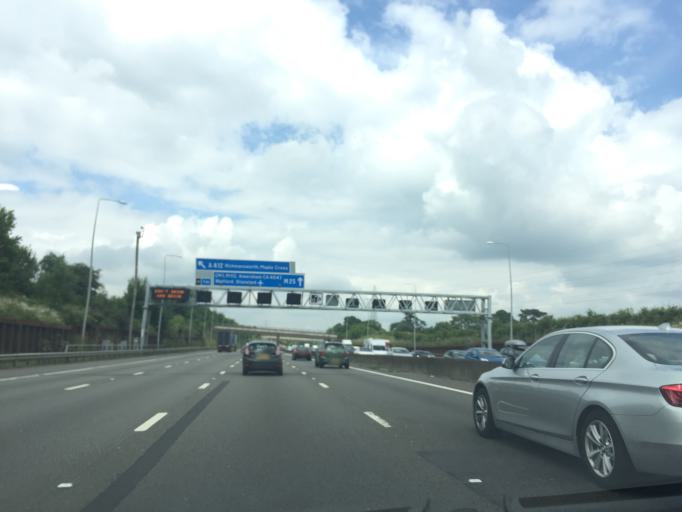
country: GB
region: England
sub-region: Buckinghamshire
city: Chalfont Saint Peter
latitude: 51.6182
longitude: -0.5258
